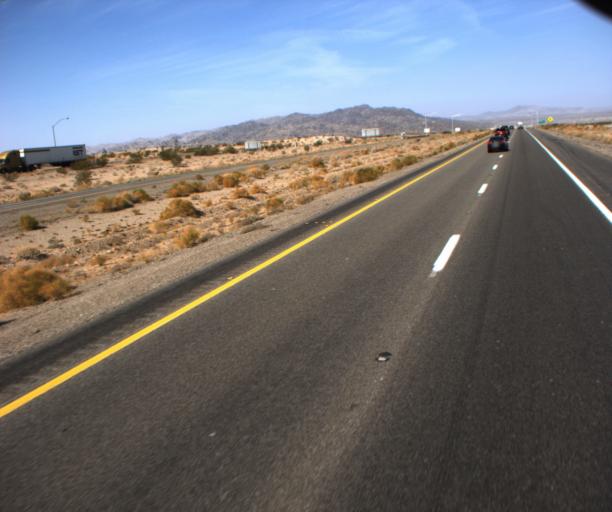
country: US
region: Arizona
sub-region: Mohave County
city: Desert Hills
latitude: 34.7239
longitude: -114.4215
